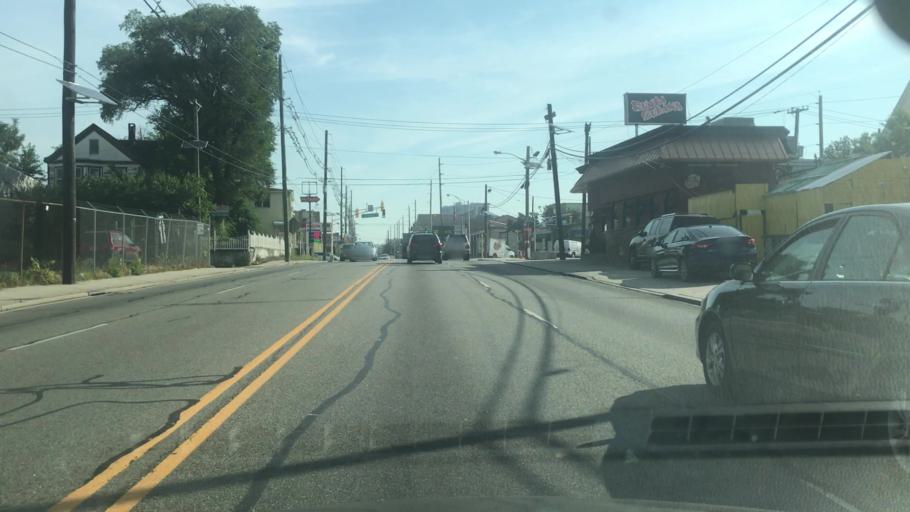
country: US
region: New Jersey
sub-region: Hudson County
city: Union City
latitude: 40.7839
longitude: -74.0341
